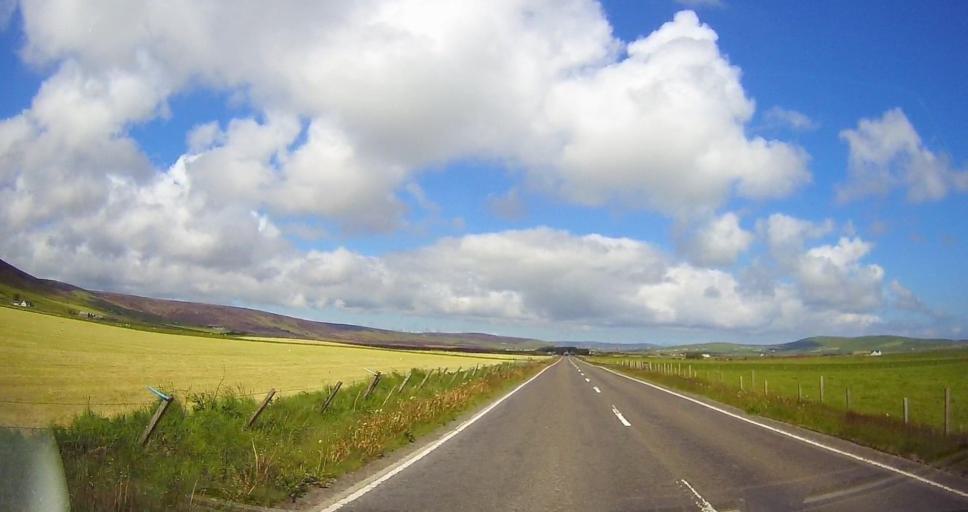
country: GB
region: Scotland
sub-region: Orkney Islands
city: Orkney
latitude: 59.0364
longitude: -3.0893
